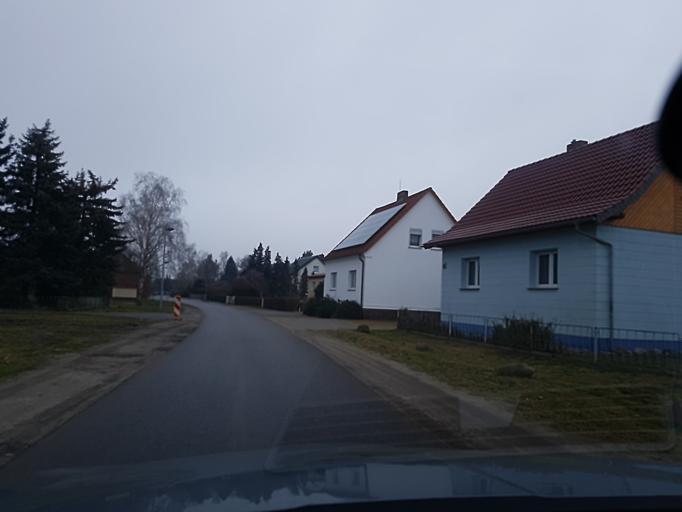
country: DE
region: Brandenburg
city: Schonewalde
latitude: 51.6571
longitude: 13.5998
